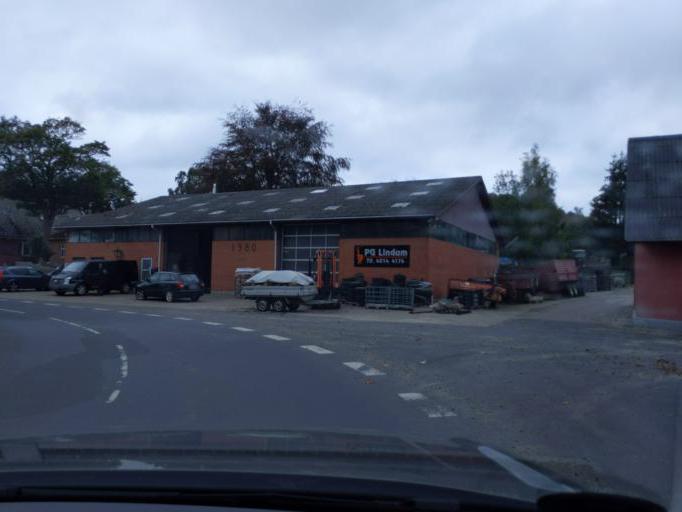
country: DK
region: North Denmark
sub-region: Mariagerfjord Kommune
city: Hobro
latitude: 56.5618
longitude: 9.6854
